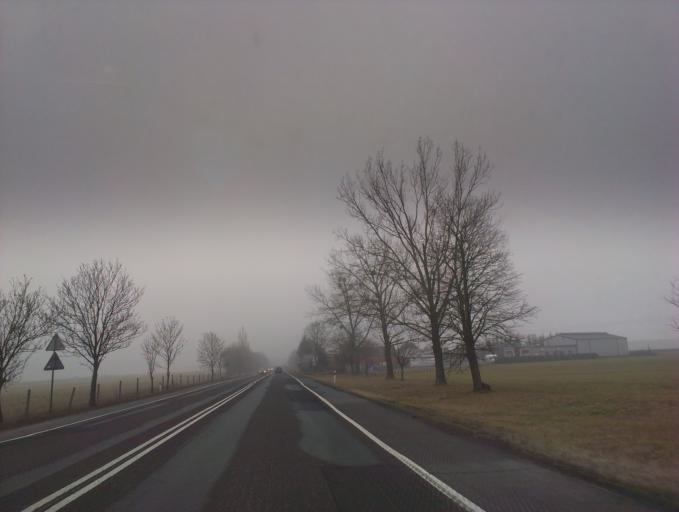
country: PL
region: Greater Poland Voivodeship
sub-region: Powiat pilski
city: Ujscie
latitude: 53.0385
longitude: 16.7702
